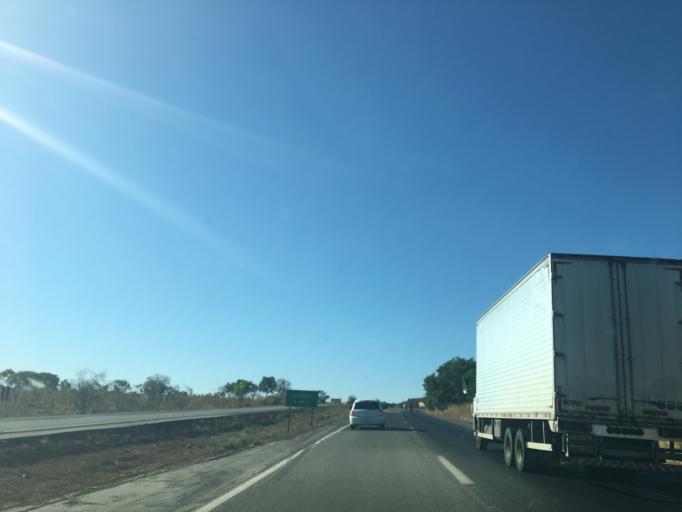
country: BR
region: Goias
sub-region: Hidrolandia
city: Hidrolandia
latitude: -17.0655
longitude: -49.2249
